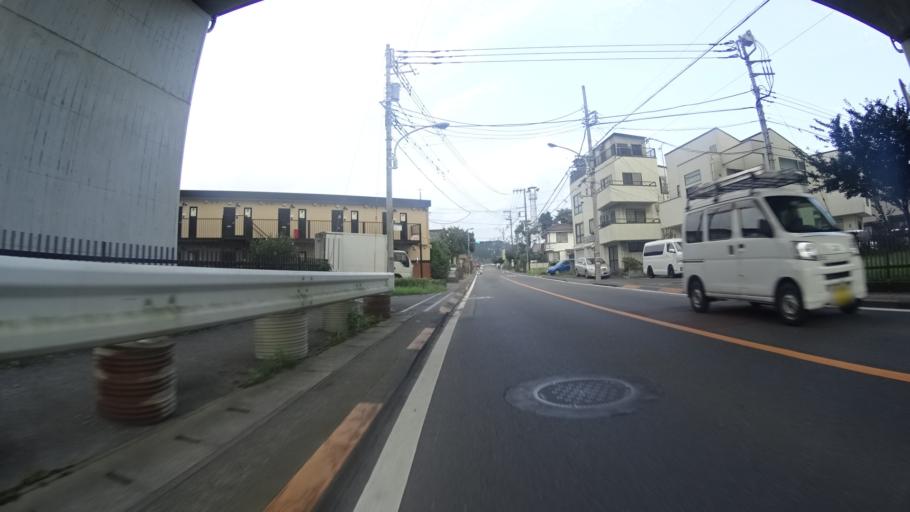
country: JP
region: Tokyo
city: Fussa
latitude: 35.7714
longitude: 139.2901
